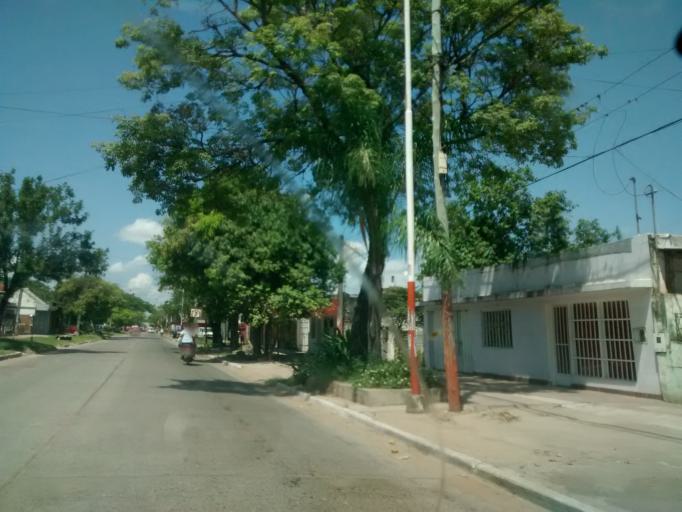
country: AR
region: Chaco
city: Resistencia
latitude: -27.4655
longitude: -58.9740
